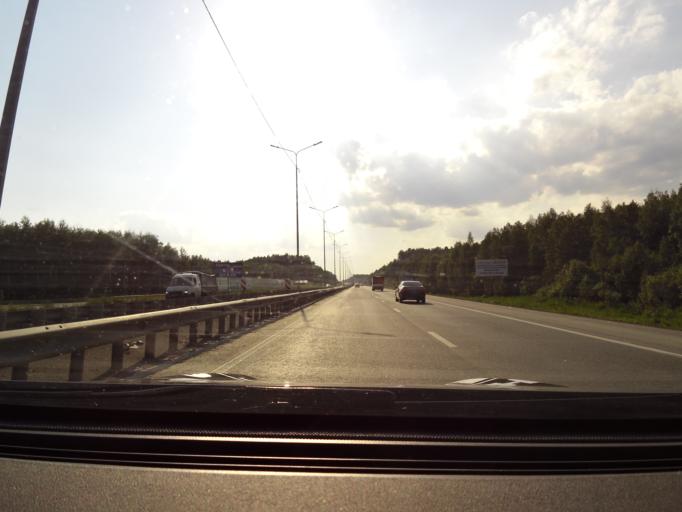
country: RU
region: Sverdlovsk
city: Shirokaya Rechka
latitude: 56.8292
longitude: 60.4133
